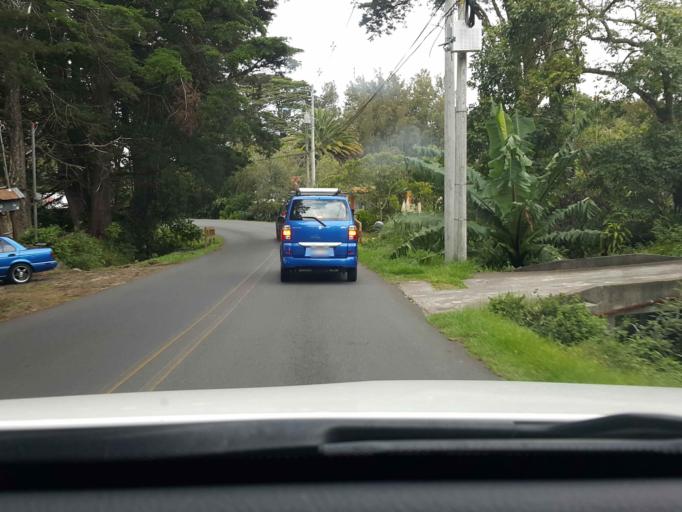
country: CR
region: Heredia
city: San Josecito
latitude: 10.0513
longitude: -84.0869
